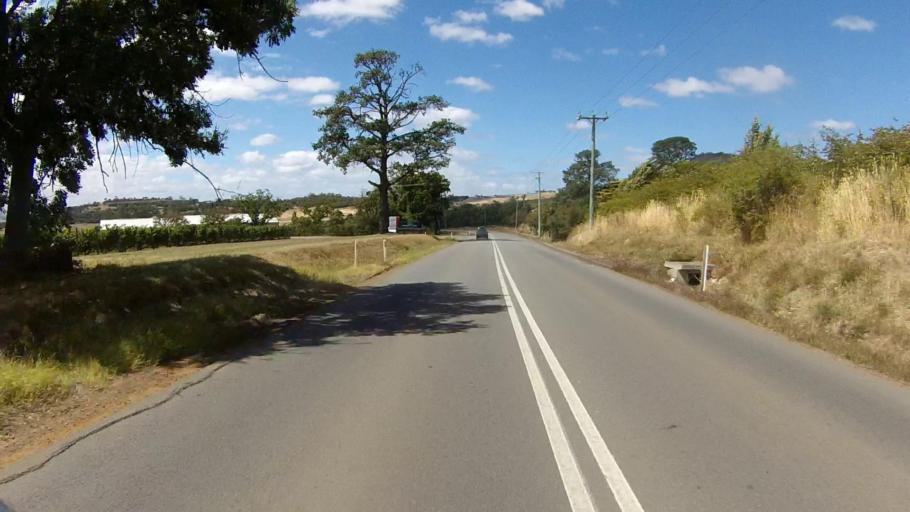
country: AU
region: Tasmania
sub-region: Clarence
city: Cambridge
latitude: -42.8093
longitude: 147.4265
